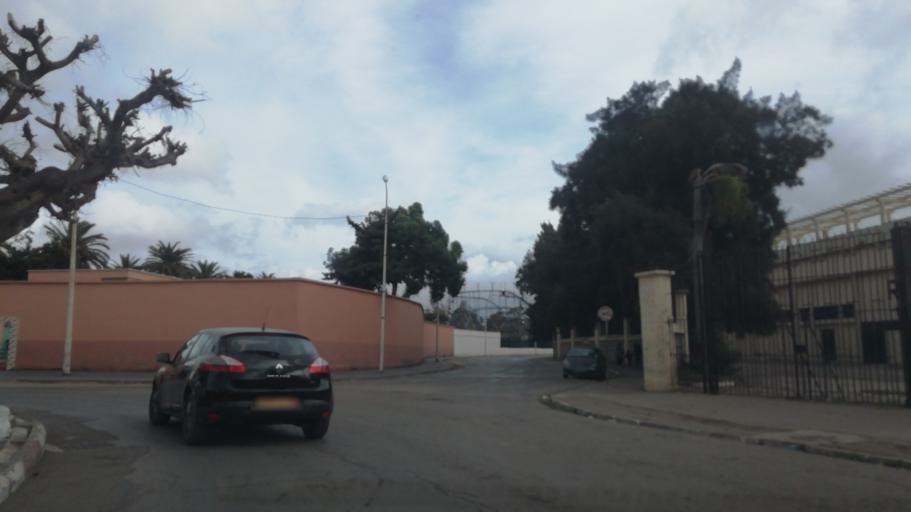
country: DZ
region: Oran
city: Oran
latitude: 35.6847
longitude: -0.6367
